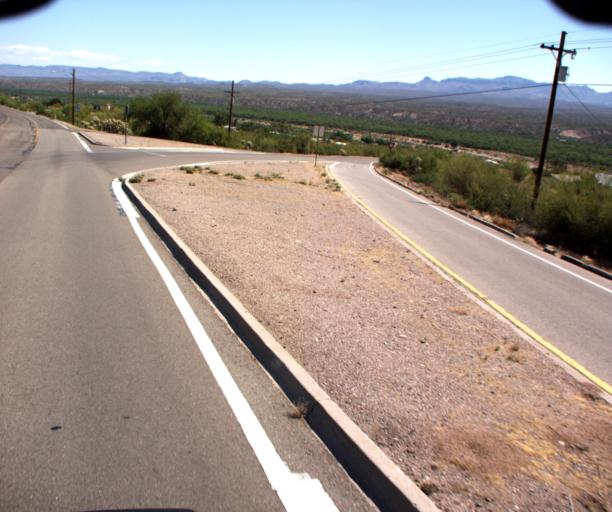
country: US
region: Arizona
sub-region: Pinal County
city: Mammoth
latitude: 32.7119
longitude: -110.6414
